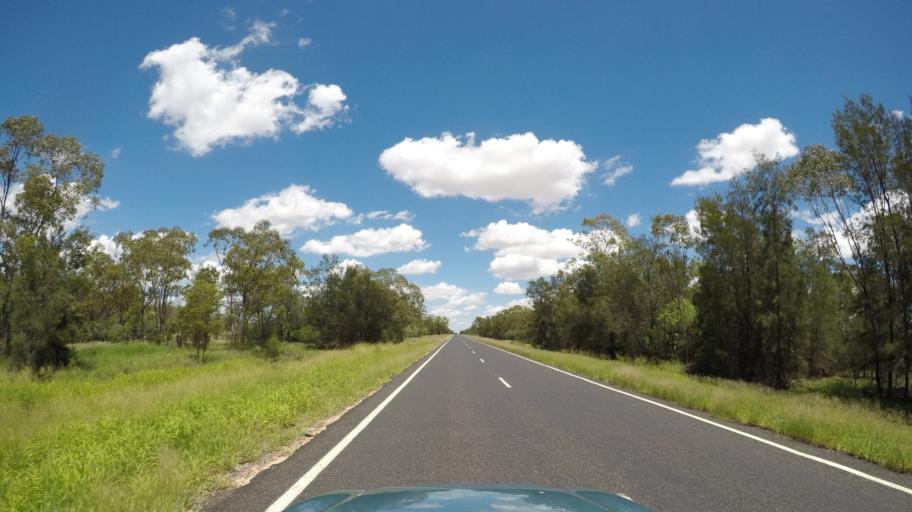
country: AU
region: Queensland
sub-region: Goondiwindi
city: Goondiwindi
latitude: -28.1671
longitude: 150.5986
